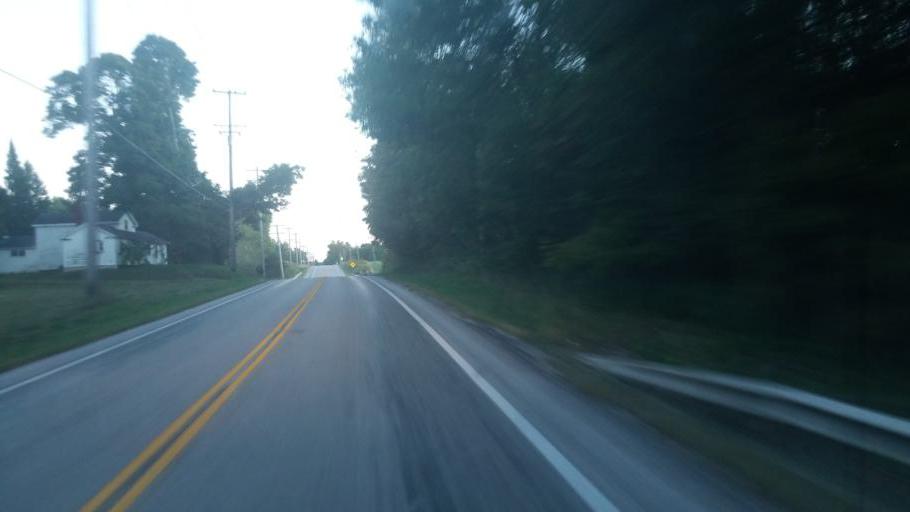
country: US
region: Ohio
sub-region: Ashtabula County
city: Andover
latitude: 41.7687
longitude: -80.5719
